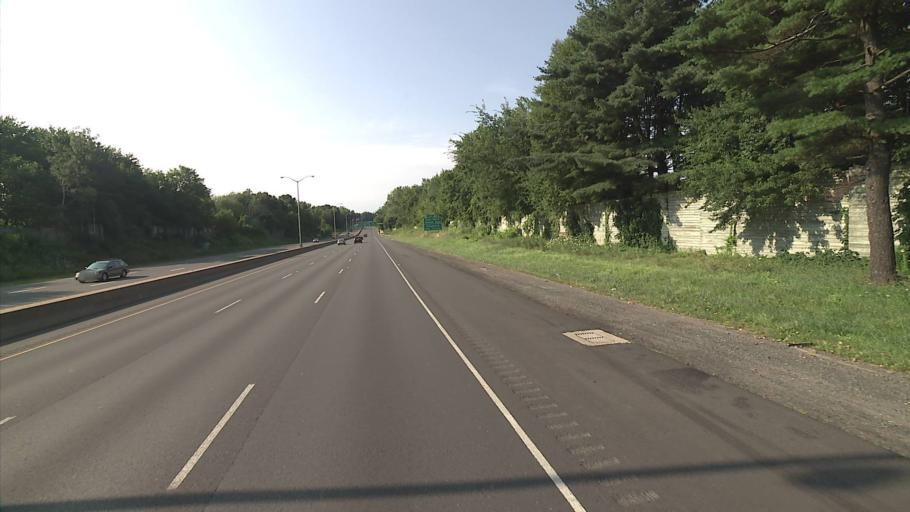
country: US
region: Connecticut
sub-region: Hartford County
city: Thompsonville
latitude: 42.0103
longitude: -72.5861
